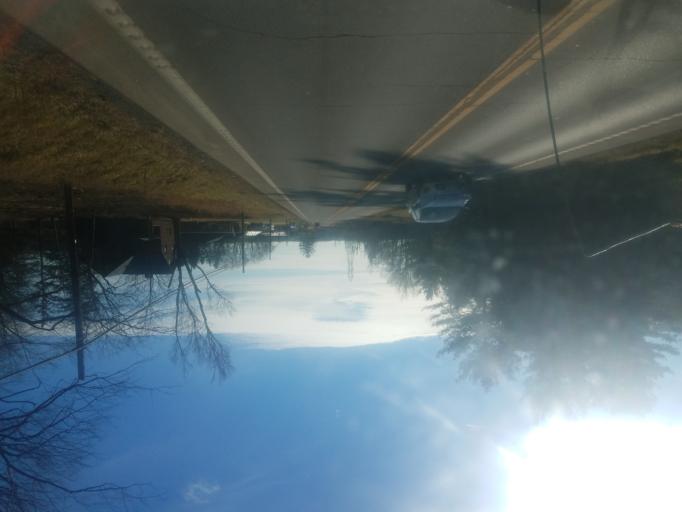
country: US
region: Ohio
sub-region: Richland County
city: Lexington
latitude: 40.7005
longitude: -82.5591
